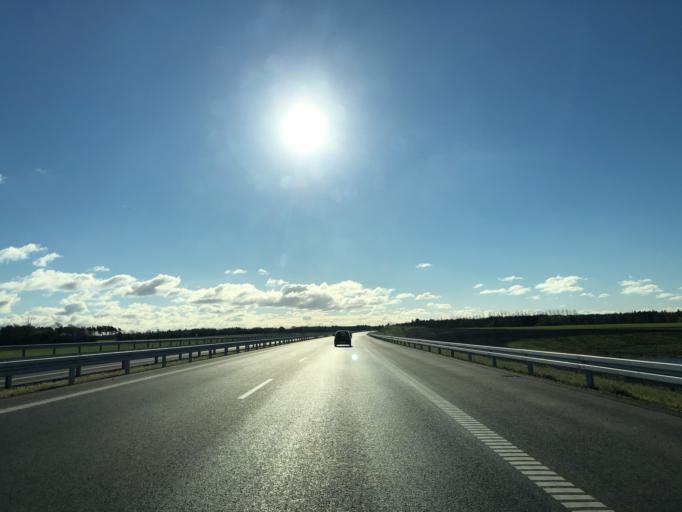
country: DK
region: Central Jutland
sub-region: Herning Kommune
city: Avlum
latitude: 56.3473
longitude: 8.7376
